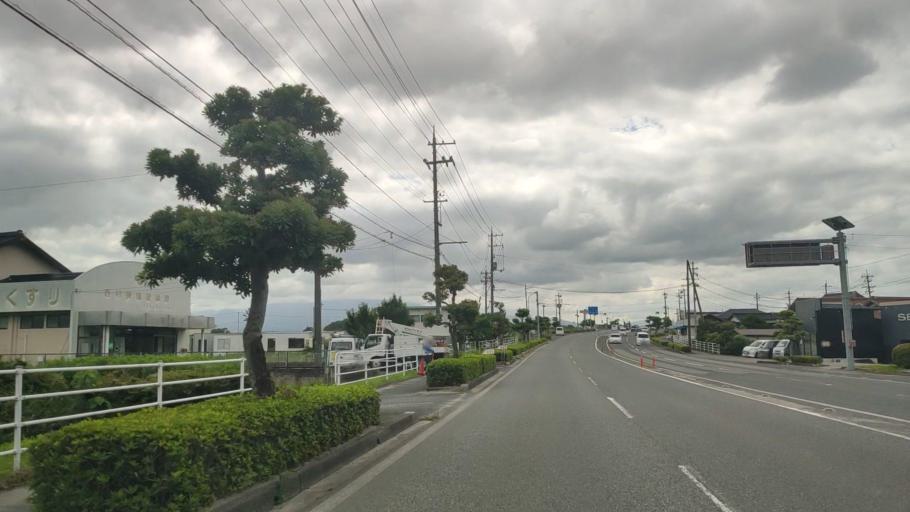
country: JP
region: Tottori
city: Yonago
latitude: 35.4095
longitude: 133.3608
